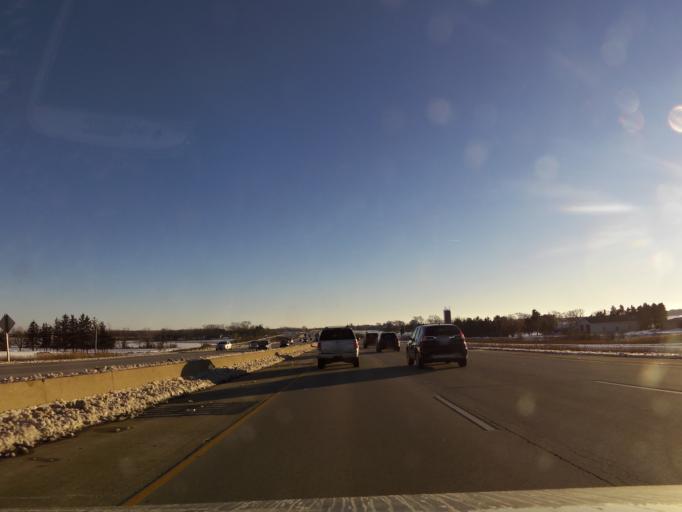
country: US
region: Wisconsin
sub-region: Racine County
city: Sturtevant
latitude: 42.6942
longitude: -87.9539
